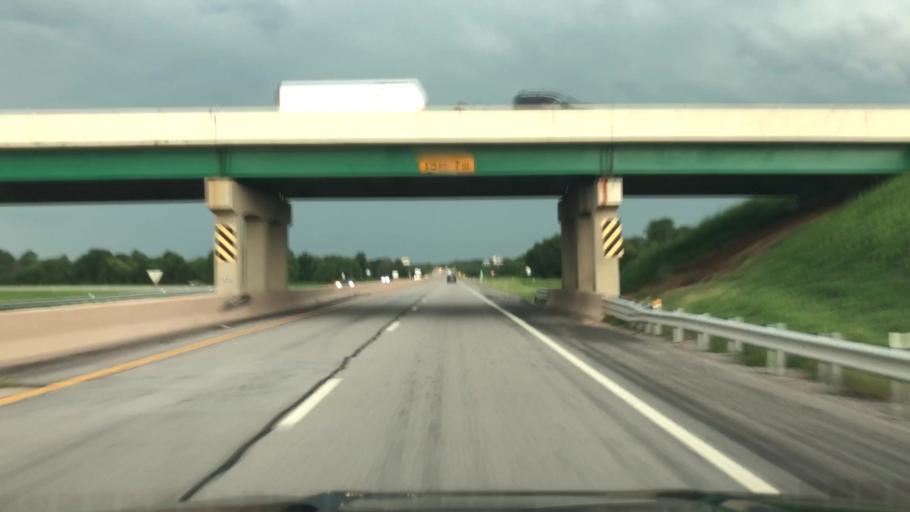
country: US
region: Oklahoma
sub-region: Rogers County
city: Justice
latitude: 36.3013
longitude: -95.5911
